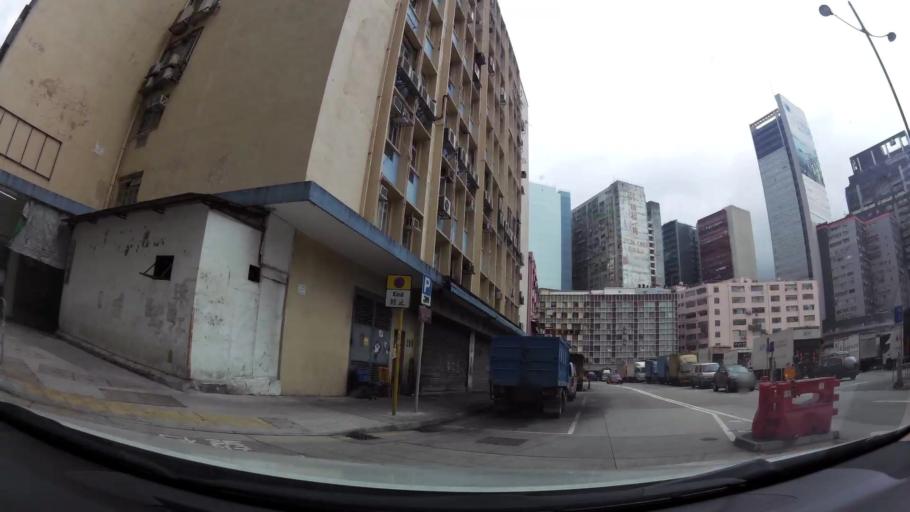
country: HK
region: Wong Tai Sin
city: Wong Tai Sin
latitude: 22.3349
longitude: 114.1986
